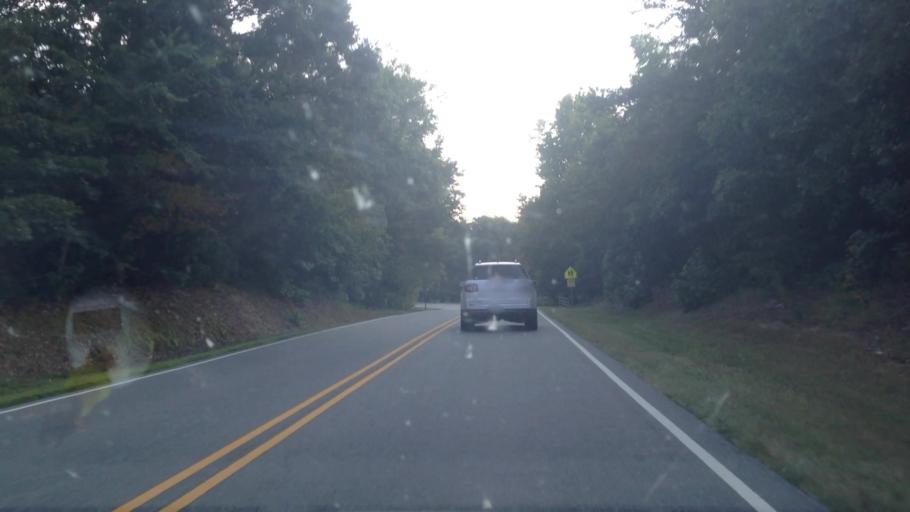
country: US
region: North Carolina
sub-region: Davidson County
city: Wallburg
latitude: 35.9732
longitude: -80.0812
